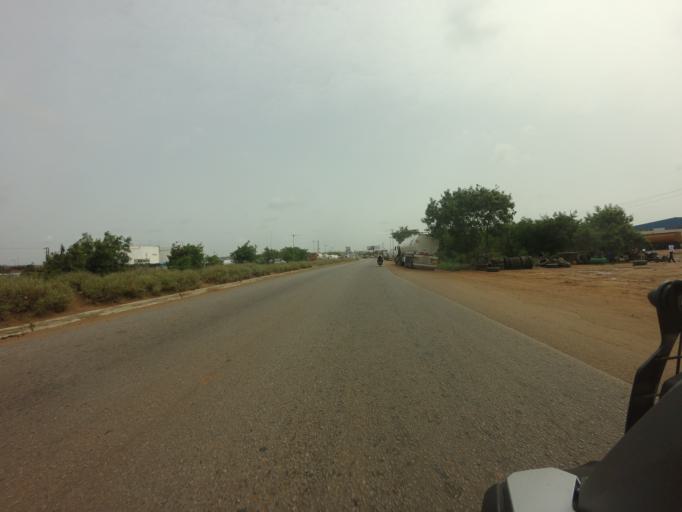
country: GH
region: Greater Accra
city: Tema
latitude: 5.7140
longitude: 0.0128
